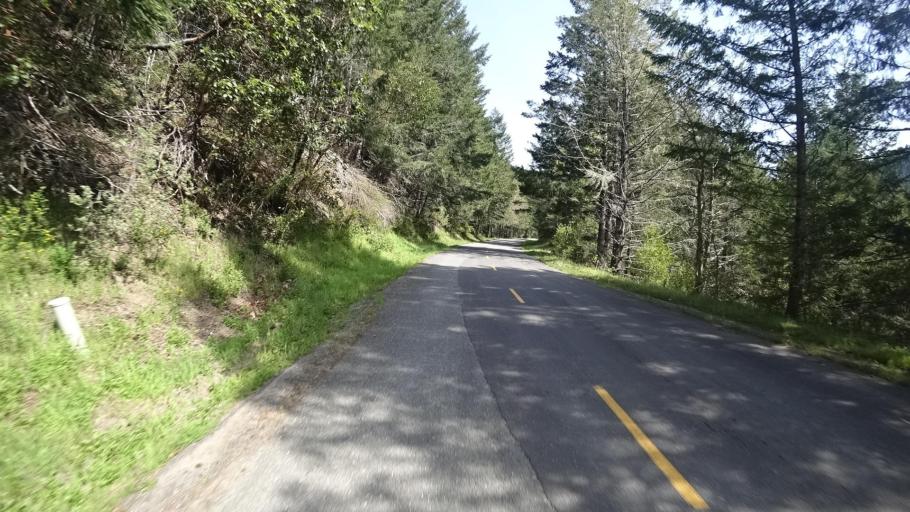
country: US
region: California
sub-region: Humboldt County
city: Rio Dell
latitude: 40.4551
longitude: -123.8018
